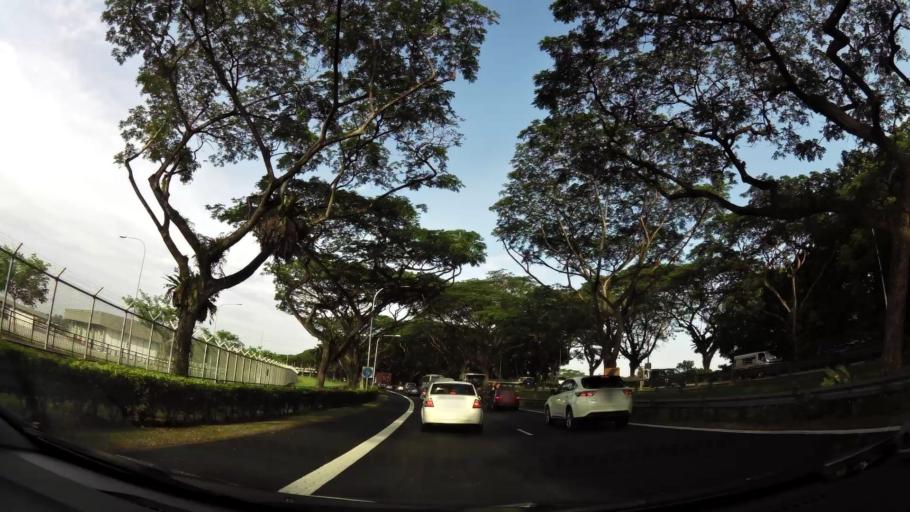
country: MY
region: Johor
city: Johor Bahru
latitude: 1.3624
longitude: 103.7080
